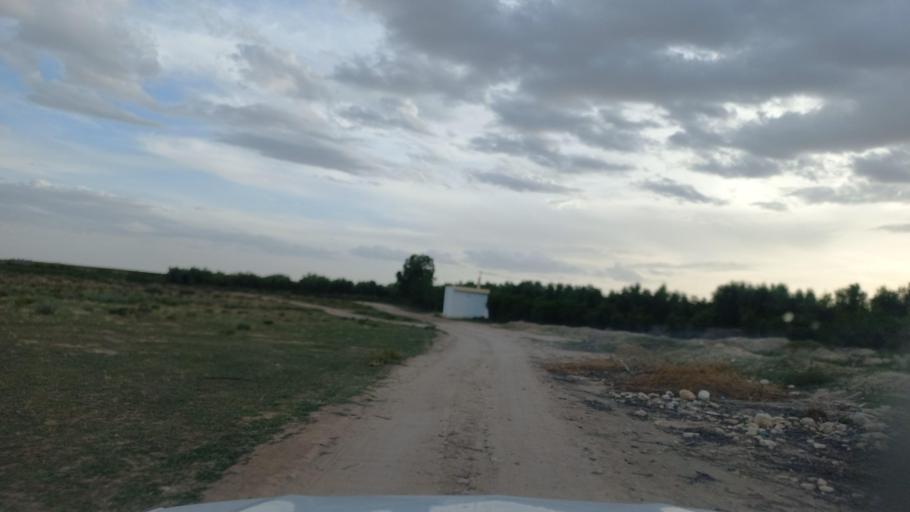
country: TN
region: Al Qasrayn
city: Sbiba
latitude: 35.4301
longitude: 9.0982
